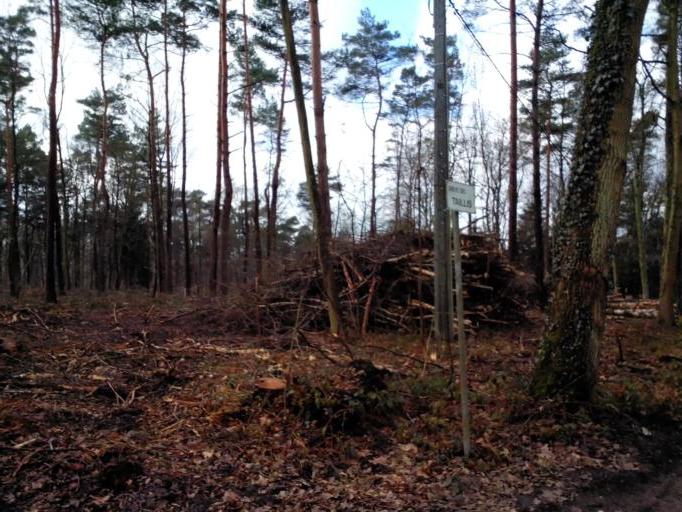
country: BE
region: Wallonia
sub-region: Province du Brabant Wallon
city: Grez-Doiceau
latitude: 50.7657
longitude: 4.6564
